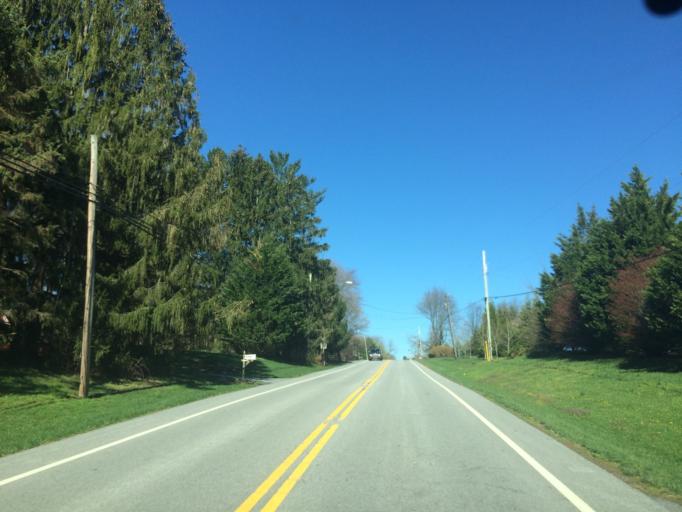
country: US
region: Maryland
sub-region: Carroll County
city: Mount Airy
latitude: 39.3382
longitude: -77.0775
